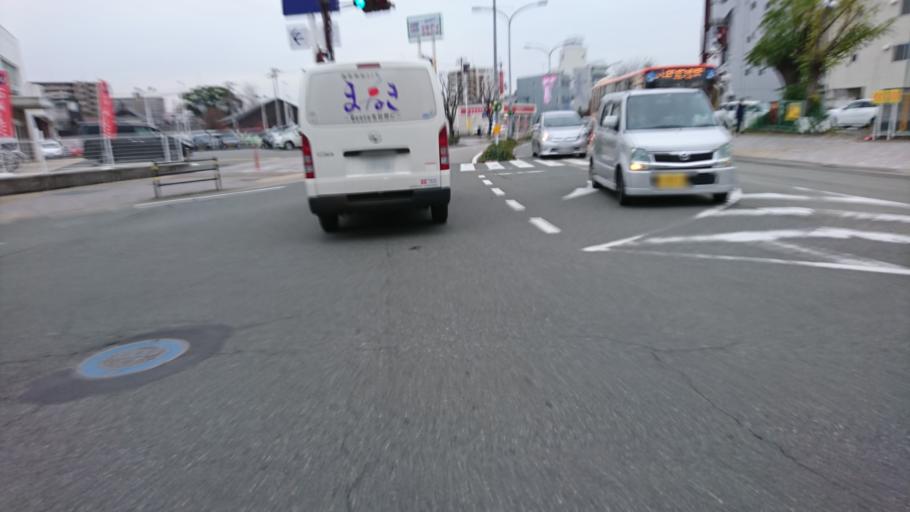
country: JP
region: Hyogo
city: Kakogawacho-honmachi
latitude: 34.7643
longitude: 134.8409
